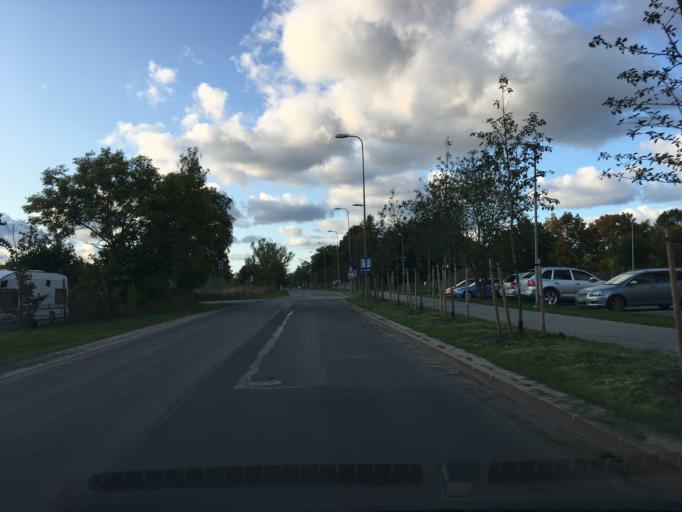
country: EE
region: Harju
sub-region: Tallinna linn
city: Kose
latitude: 59.4441
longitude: 24.8280
